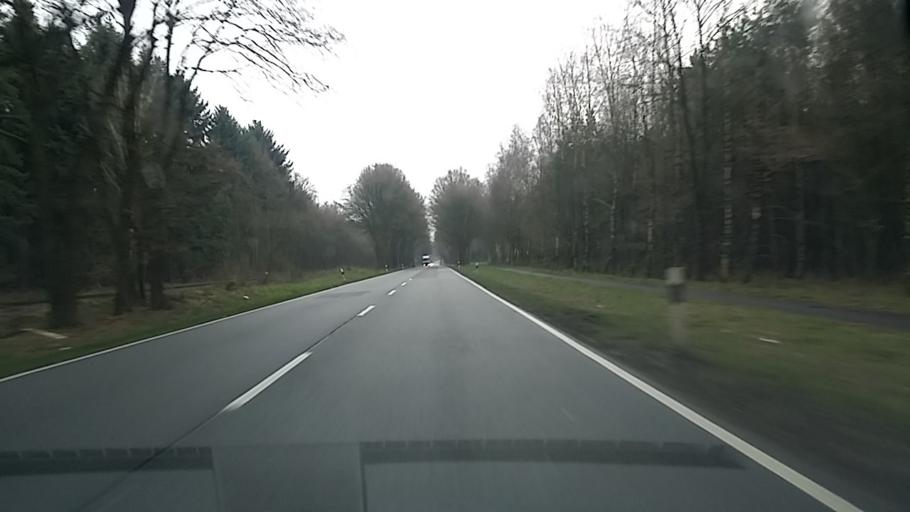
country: DE
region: Lower Saxony
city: Herzlake
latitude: 52.6986
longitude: 7.6250
